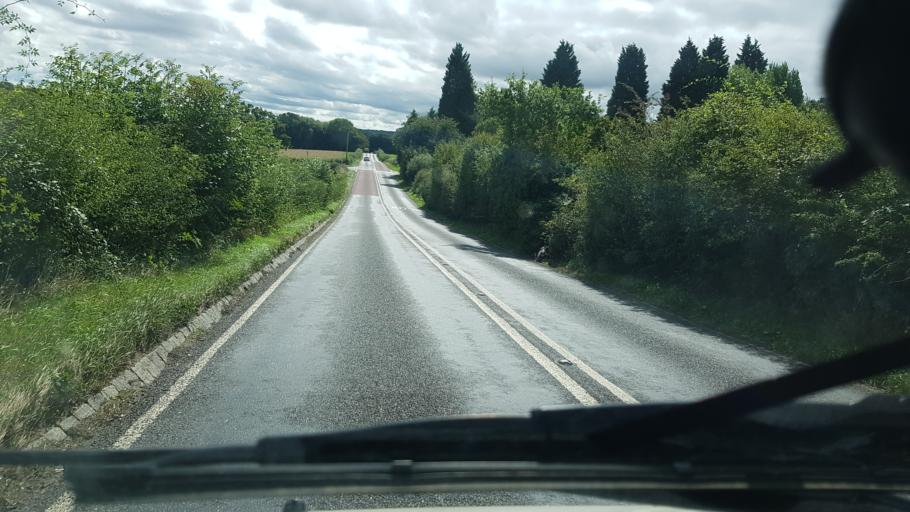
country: GB
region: England
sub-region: West Sussex
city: Rudgwick
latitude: 51.0918
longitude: -0.4734
